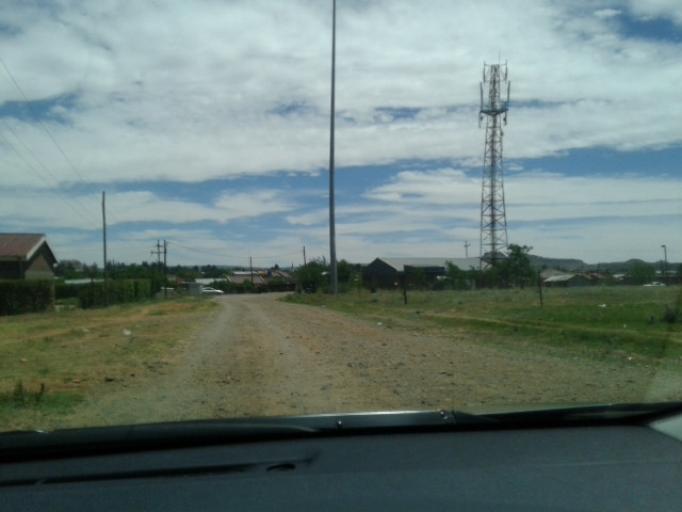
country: LS
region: Maseru
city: Maseru
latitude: -29.2946
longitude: 27.5358
